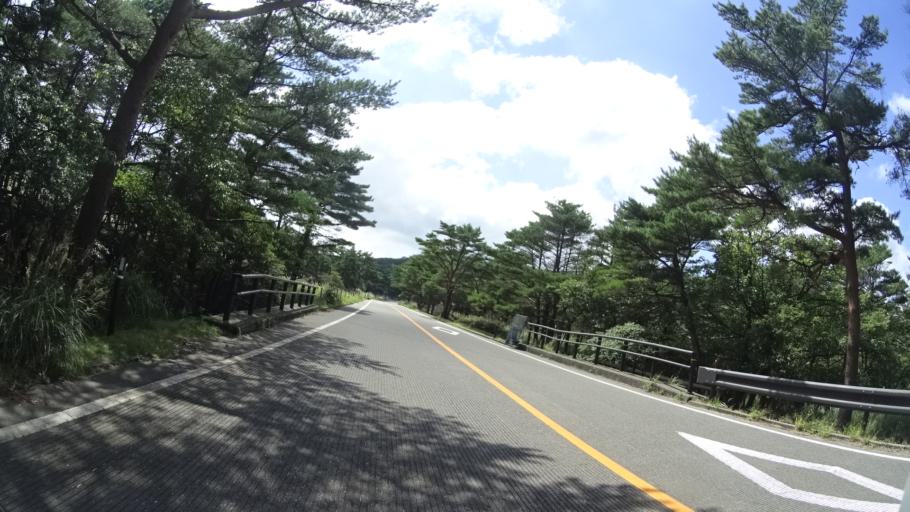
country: JP
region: Miyazaki
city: Kobayashi
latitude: 31.9446
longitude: 130.8428
